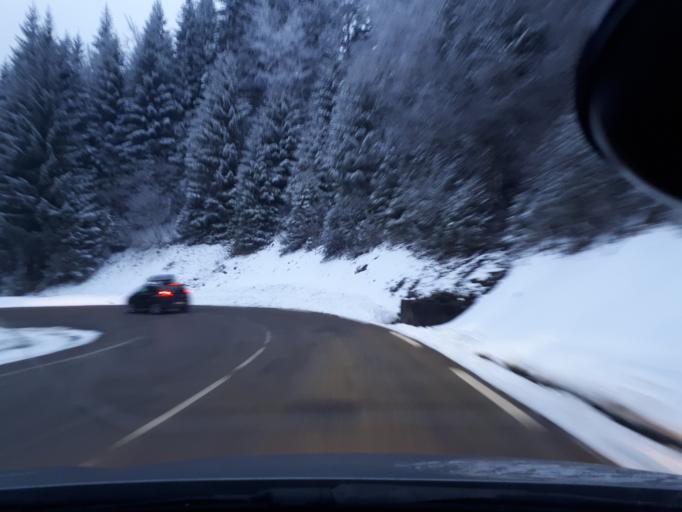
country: FR
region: Rhone-Alpes
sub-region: Departement de l'Isere
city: Vaulnaveys-le-Bas
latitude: 45.1031
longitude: 5.8514
